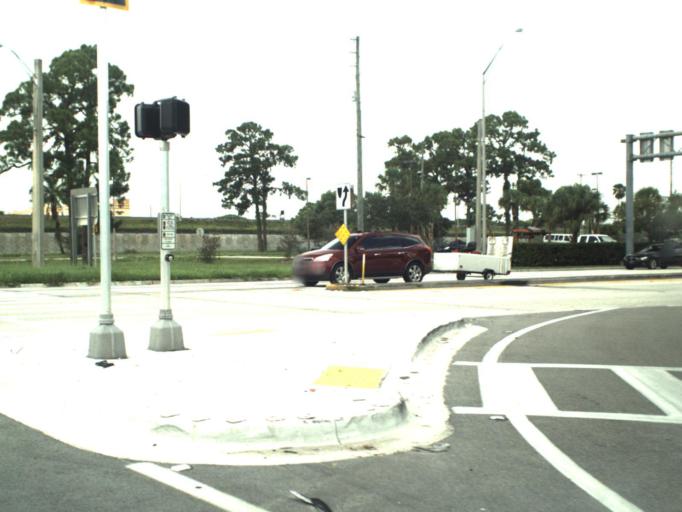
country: US
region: Florida
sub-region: Palm Beach County
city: Greenacres City
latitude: 26.6176
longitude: -80.1717
